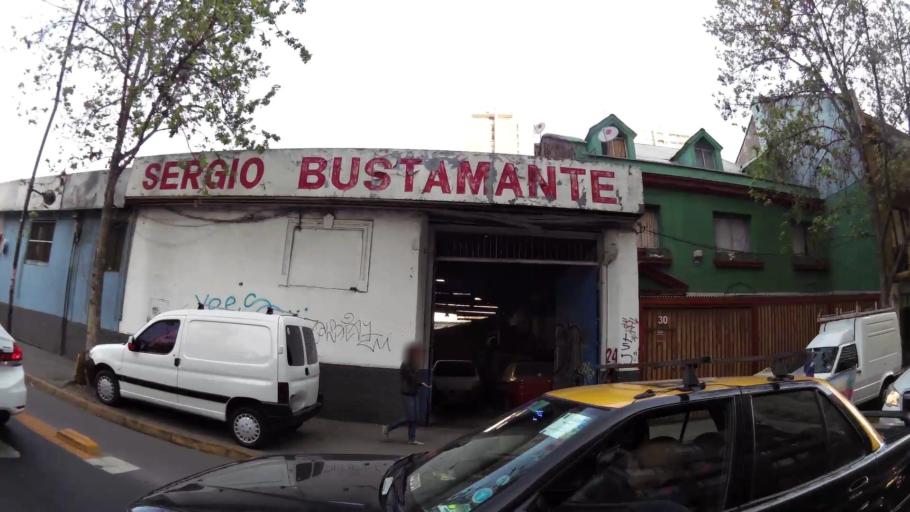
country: CL
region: Santiago Metropolitan
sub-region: Provincia de Santiago
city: Santiago
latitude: -33.4475
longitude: -70.6328
